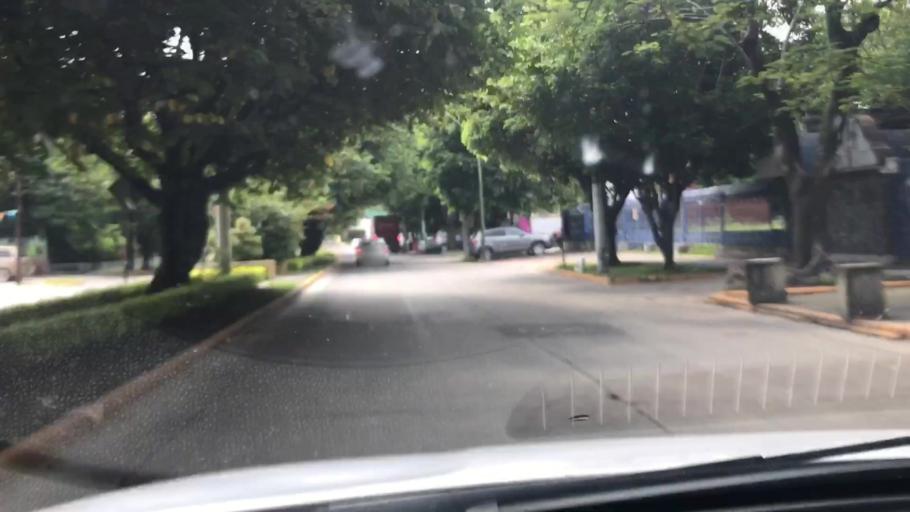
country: MX
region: Jalisco
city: Guadalajara
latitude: 20.6604
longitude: -103.3988
